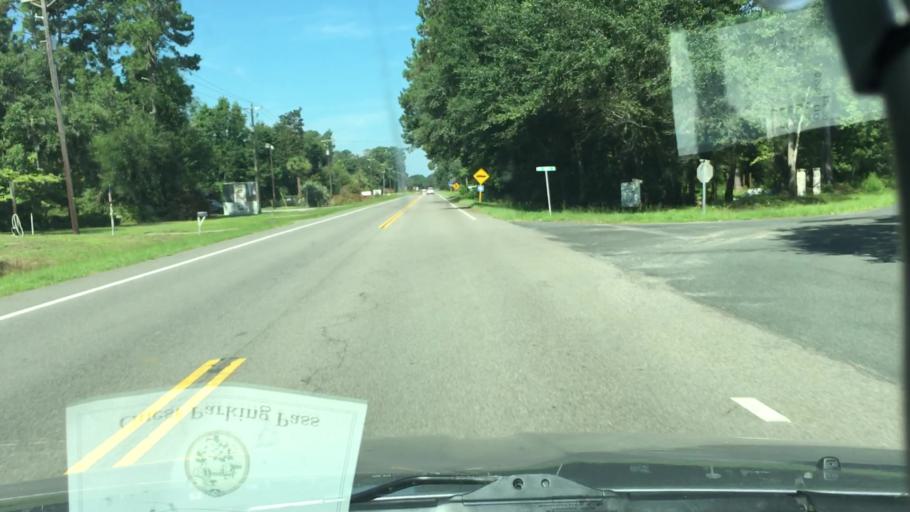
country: US
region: South Carolina
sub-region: Beaufort County
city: Beaufort
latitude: 32.4133
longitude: -80.5065
